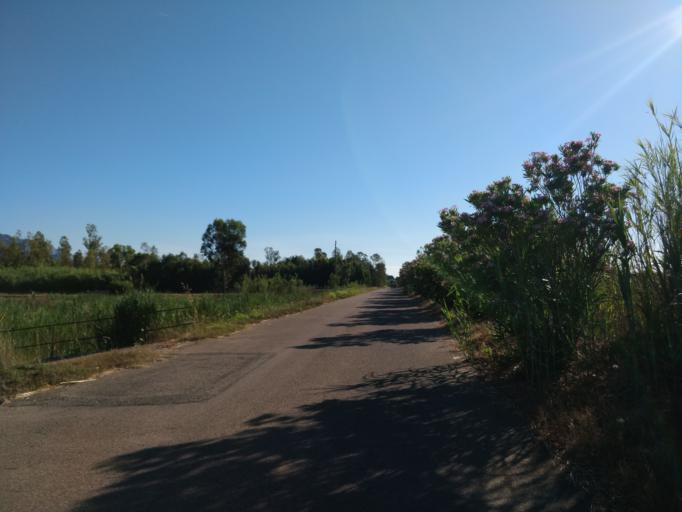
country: IT
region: Sardinia
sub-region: Provincia di Ogliastra
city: Girasole
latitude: 39.9560
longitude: 9.6740
